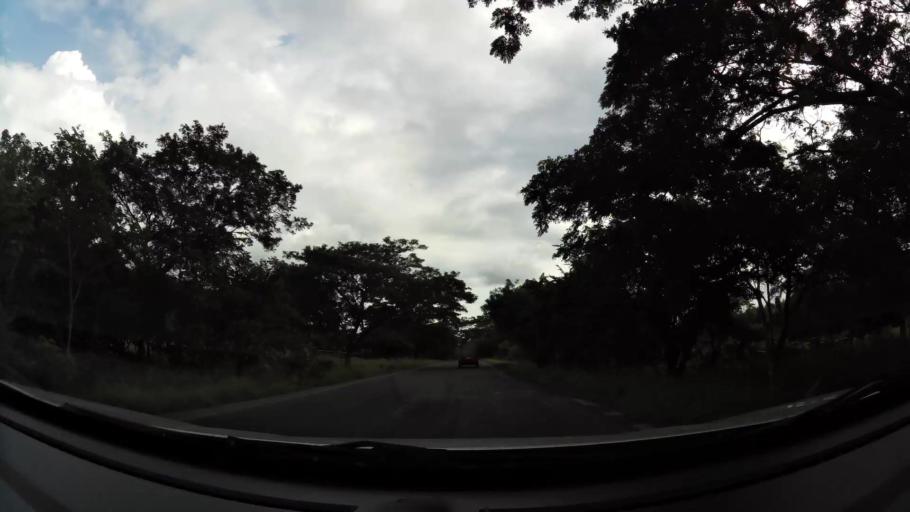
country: CR
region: Guanacaste
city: Juntas
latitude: 10.2306
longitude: -84.9801
